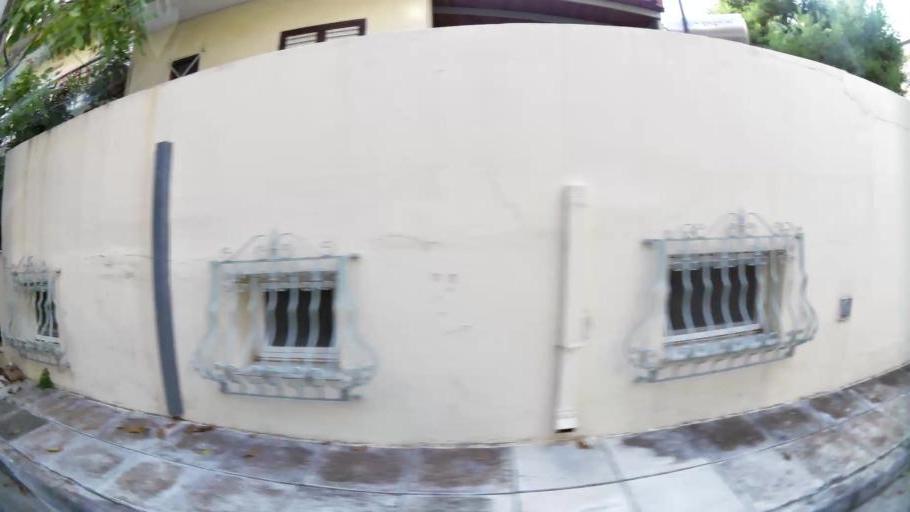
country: GR
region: Attica
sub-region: Nomarchia Athinas
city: Kamateron
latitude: 38.0584
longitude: 23.6990
